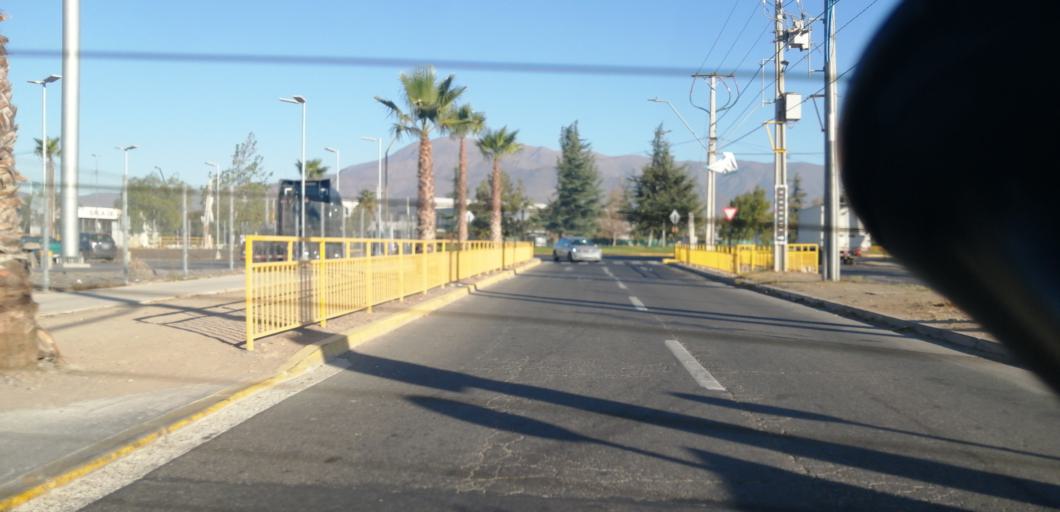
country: CL
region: Santiago Metropolitan
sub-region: Provincia de Santiago
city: Lo Prado
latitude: -33.4474
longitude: -70.8443
